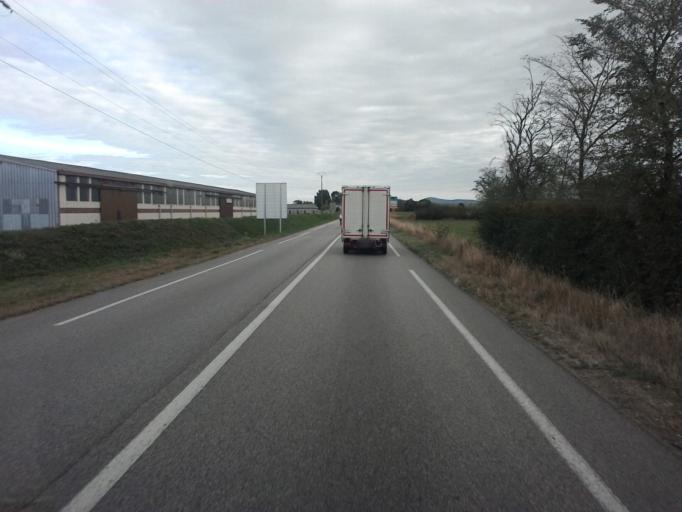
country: FR
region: Rhone-Alpes
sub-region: Departement de l'Ain
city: Ambronay
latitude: 46.0110
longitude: 5.3407
